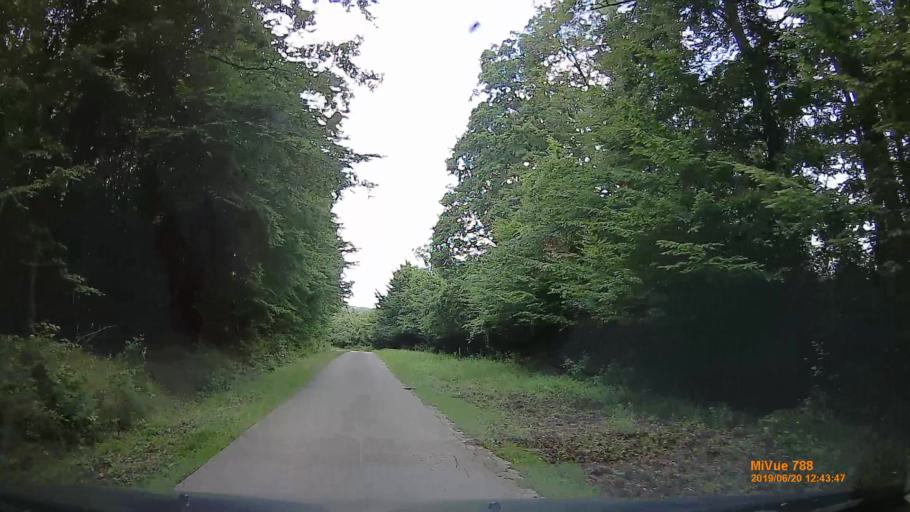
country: HU
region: Baranya
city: Hosszuheteny
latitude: 46.2027
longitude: 18.3556
